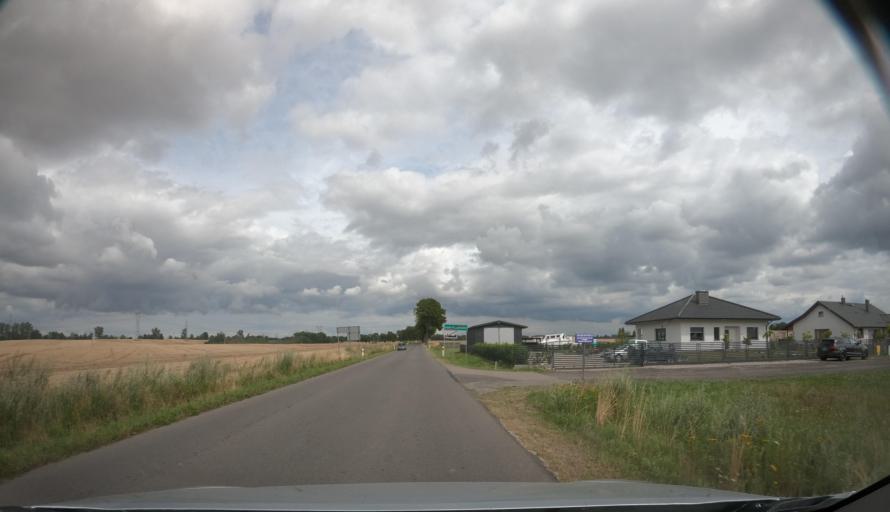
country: PL
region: West Pomeranian Voivodeship
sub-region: Koszalin
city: Koszalin
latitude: 54.1450
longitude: 16.0833
